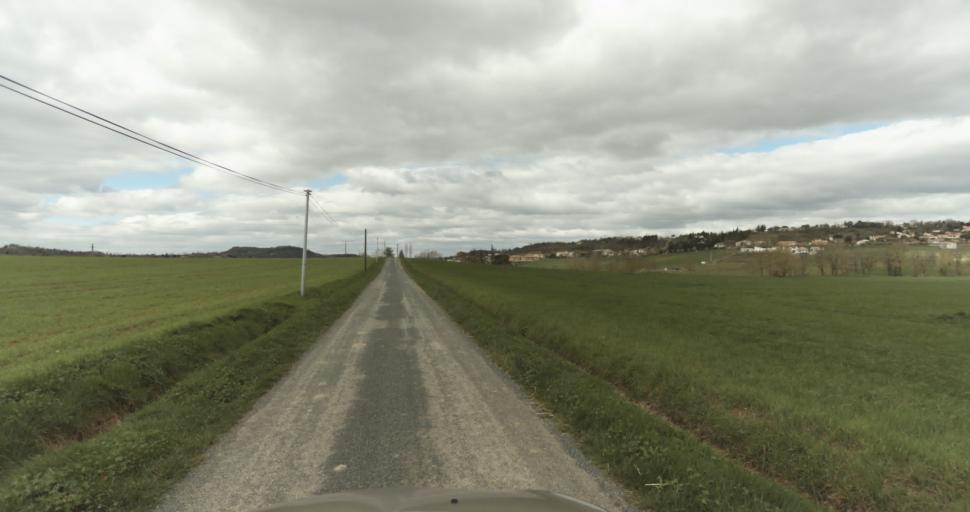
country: FR
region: Midi-Pyrenees
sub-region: Departement du Tarn
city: Puygouzon
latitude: 43.8849
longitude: 2.1752
